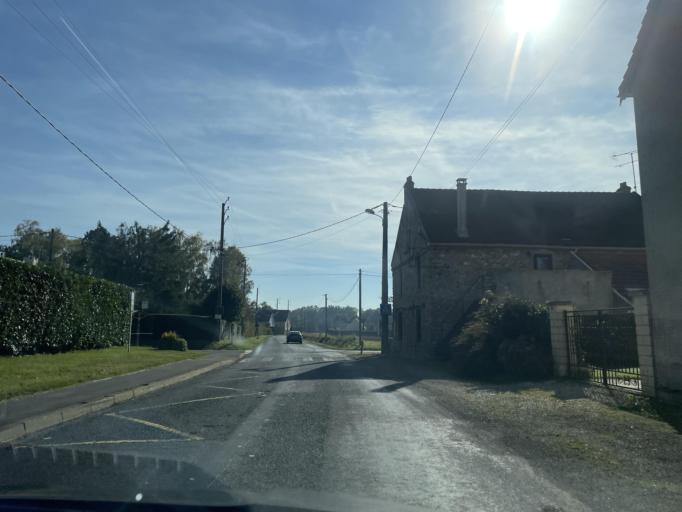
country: FR
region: Ile-de-France
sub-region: Departement de Seine-et-Marne
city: Sammeron
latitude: 48.8977
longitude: 3.0587
